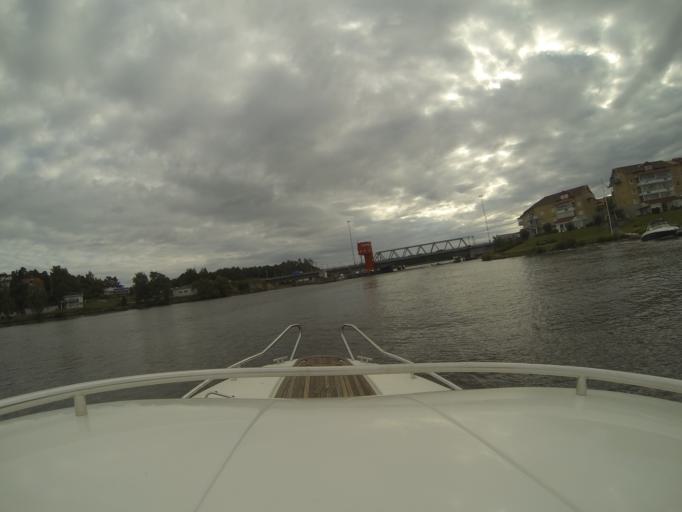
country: SE
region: Soedermanland
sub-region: Eskilstuna Kommun
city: Kvicksund
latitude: 59.4533
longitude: 16.3221
